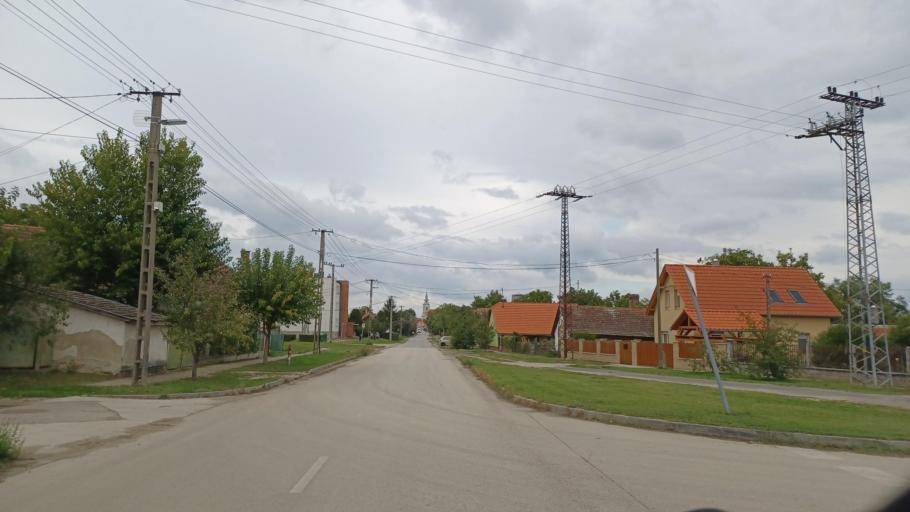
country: HU
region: Tolna
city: Simontornya
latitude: 46.7471
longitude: 18.5577
